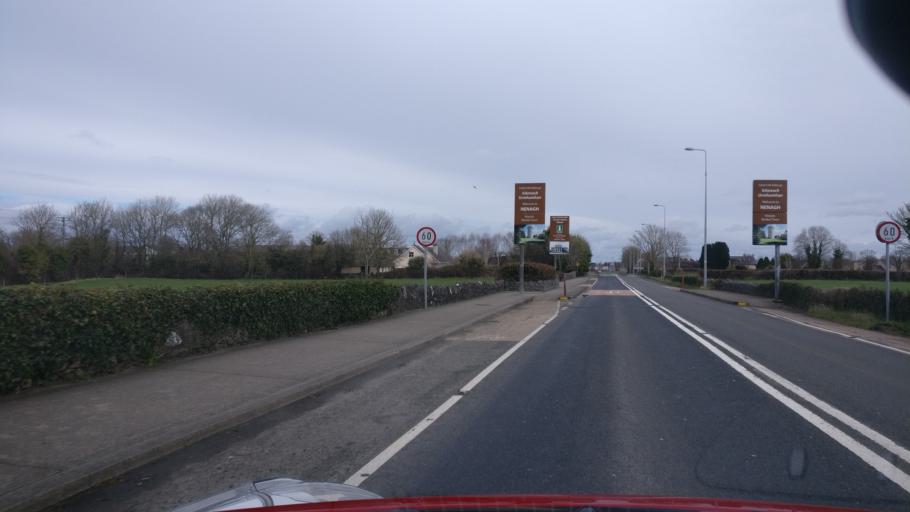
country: IE
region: Munster
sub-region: North Tipperary
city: Nenagh
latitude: 52.8583
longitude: -8.2273
